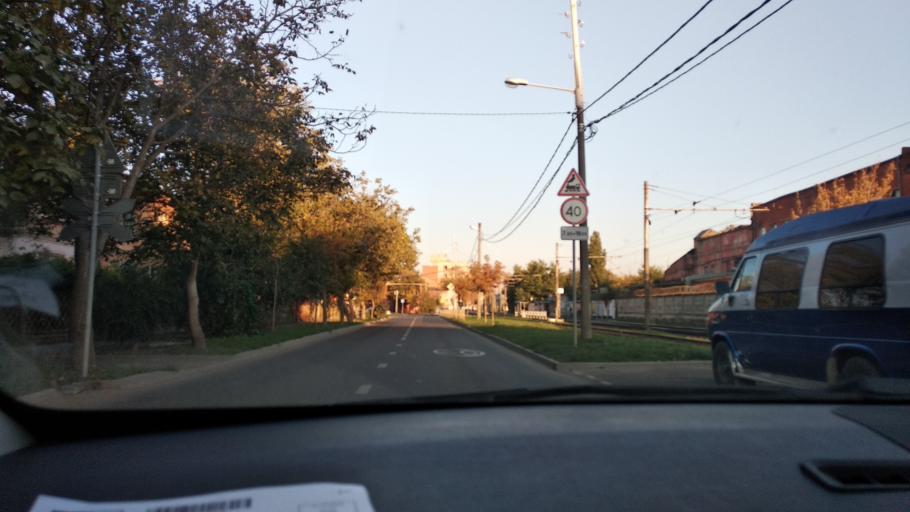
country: RU
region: Krasnodarskiy
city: Krasnodar
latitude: 45.0056
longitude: 39.0178
